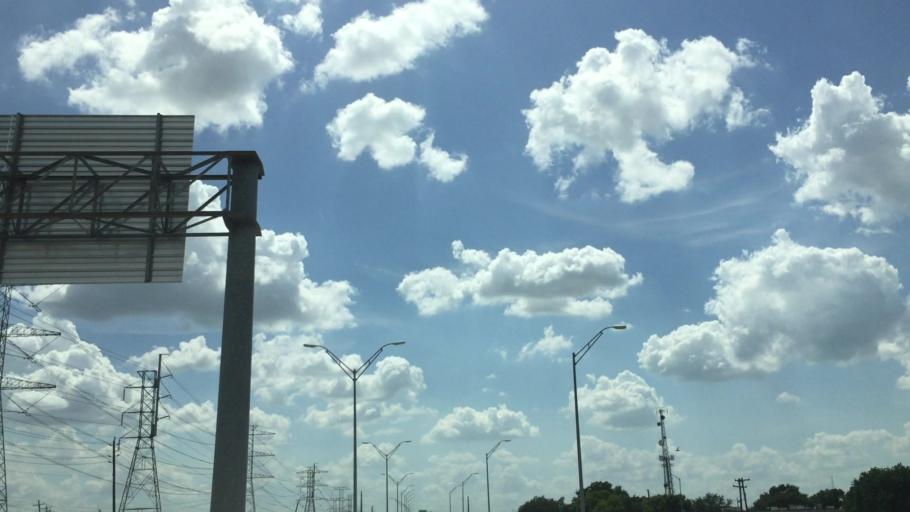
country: US
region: Texas
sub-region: Harris County
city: Piney Point Village
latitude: 29.7225
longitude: -95.5053
